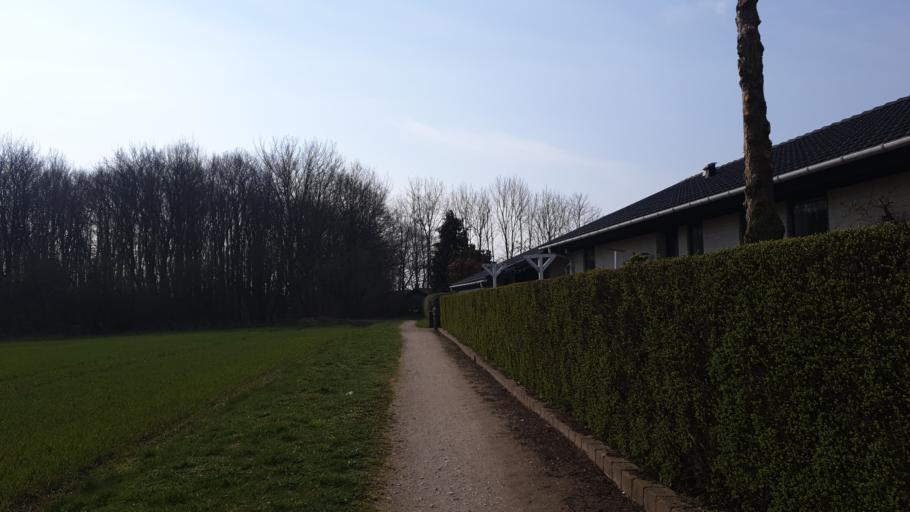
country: DK
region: Central Jutland
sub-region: Hedensted Kommune
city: Hedensted
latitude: 55.8106
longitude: 9.6914
